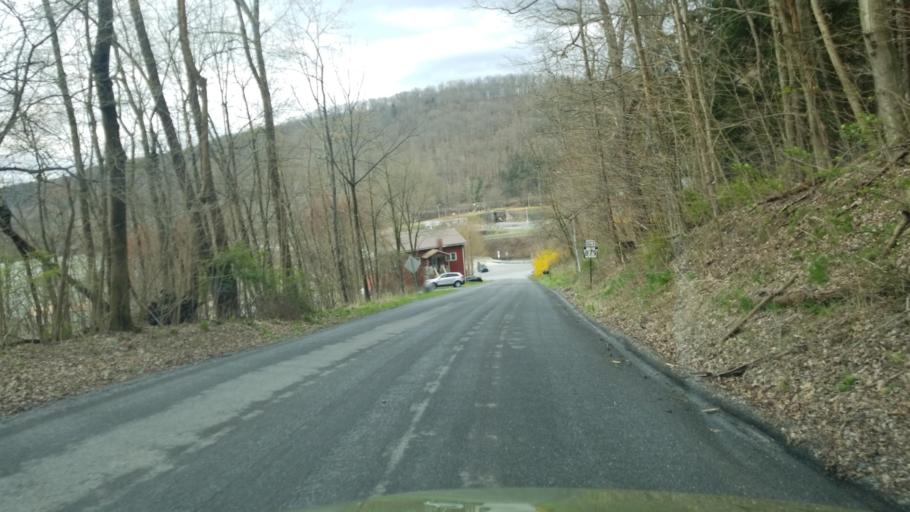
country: US
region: Pennsylvania
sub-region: Clearfield County
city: Shiloh
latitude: 41.0712
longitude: -78.3611
